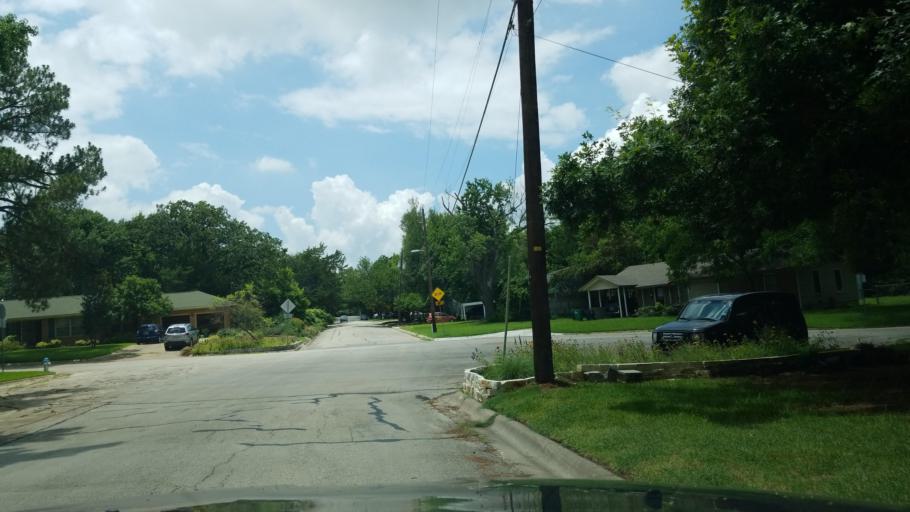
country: US
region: Texas
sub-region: Denton County
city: Denton
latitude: 33.2354
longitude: -97.1181
